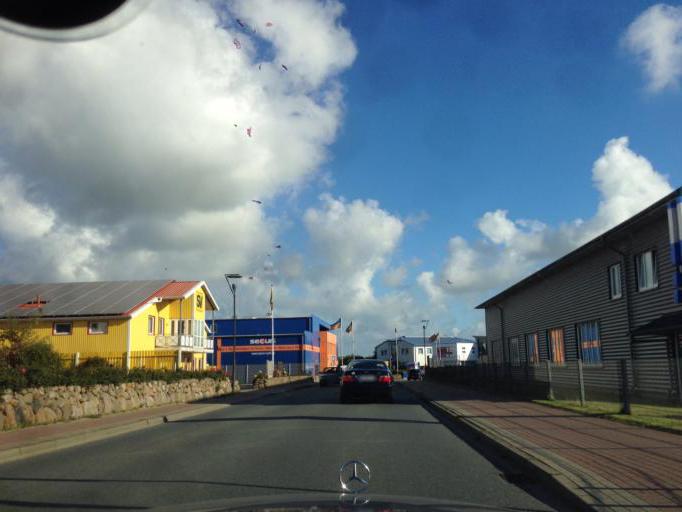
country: DE
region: Schleswig-Holstein
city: Tinnum
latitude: 54.9036
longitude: 8.3322
